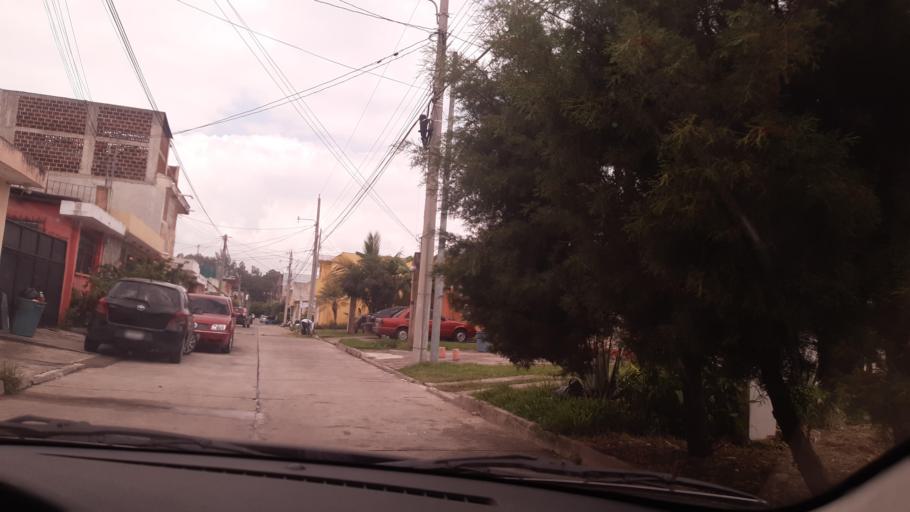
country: GT
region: Guatemala
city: Petapa
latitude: 14.5068
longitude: -90.5444
